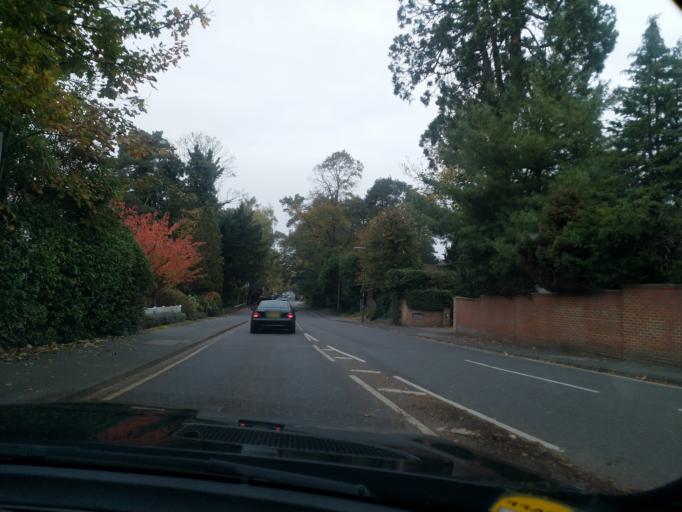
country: GB
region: England
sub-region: Surrey
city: Camberley
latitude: 51.3328
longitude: -0.7464
